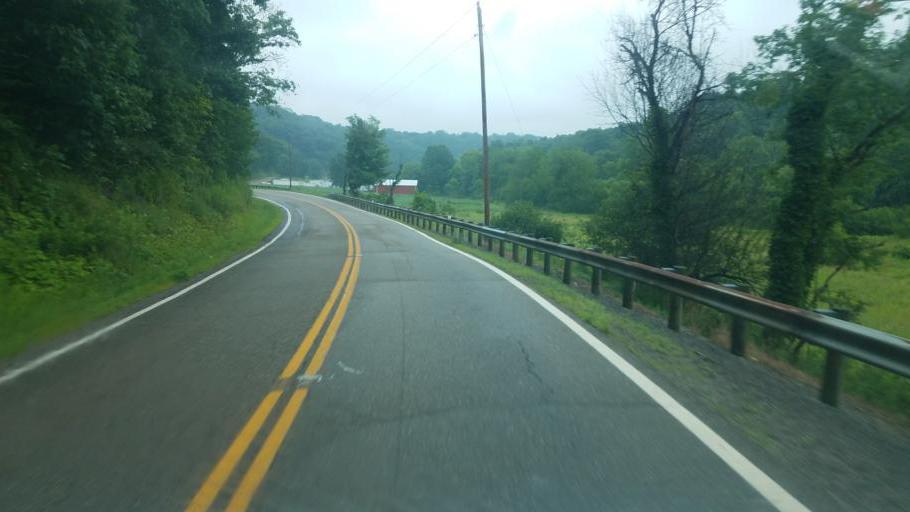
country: US
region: Ohio
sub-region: Carroll County
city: Carrollton
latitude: 40.4656
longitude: -80.9557
